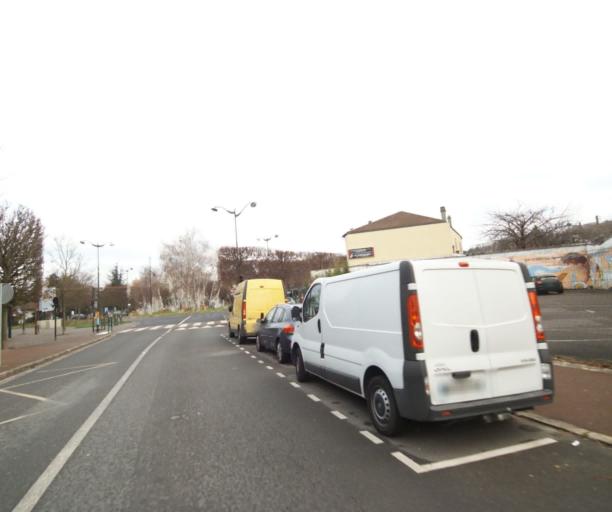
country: FR
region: Ile-de-France
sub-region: Departement des Hauts-de-Seine
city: Rueil-Malmaison
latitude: 48.8707
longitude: 2.2033
